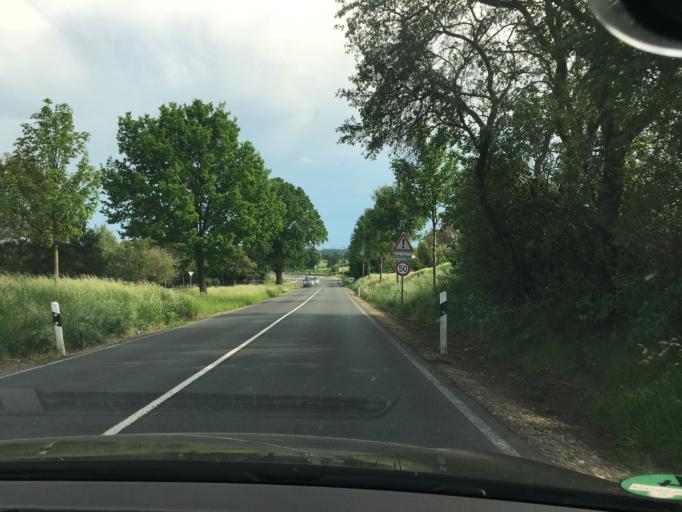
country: DE
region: North Rhine-Westphalia
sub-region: Regierungsbezirk Koln
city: Vettweiss
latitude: 50.7267
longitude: 6.5603
